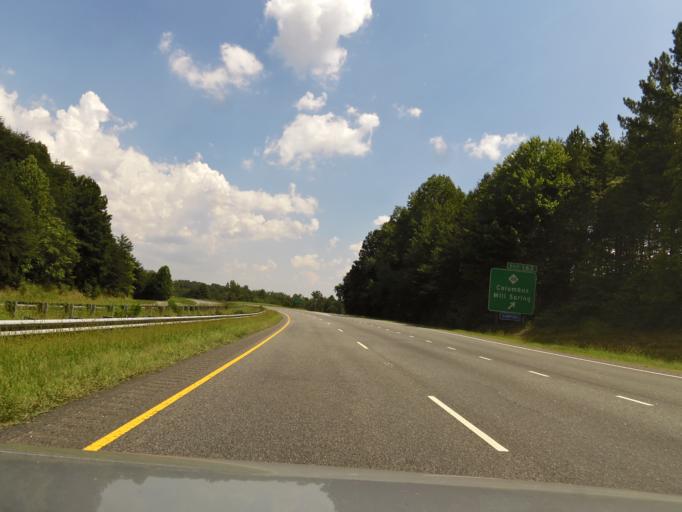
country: US
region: North Carolina
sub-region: Polk County
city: Columbus
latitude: 35.2589
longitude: -82.1882
